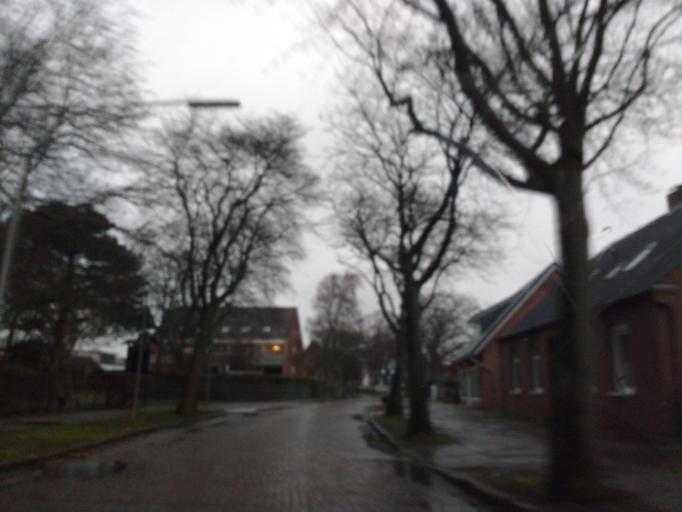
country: DE
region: Schleswig-Holstein
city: Burg auf Fehmarn
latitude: 54.4241
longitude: 11.1910
